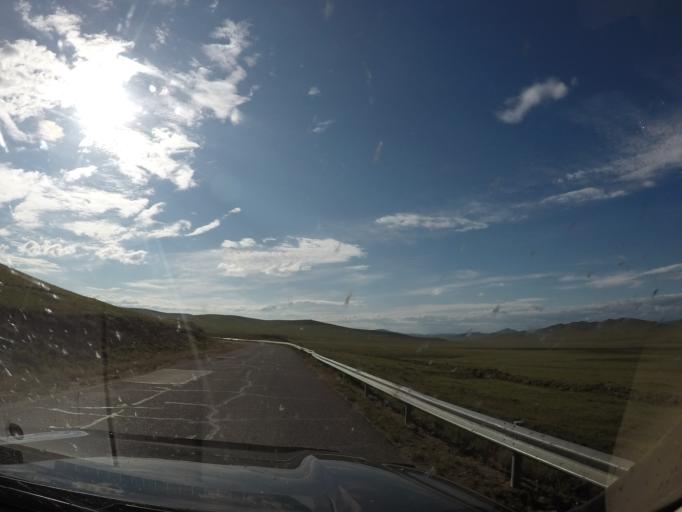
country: MN
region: Hentiy
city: Modot
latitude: 47.8101
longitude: 108.7929
